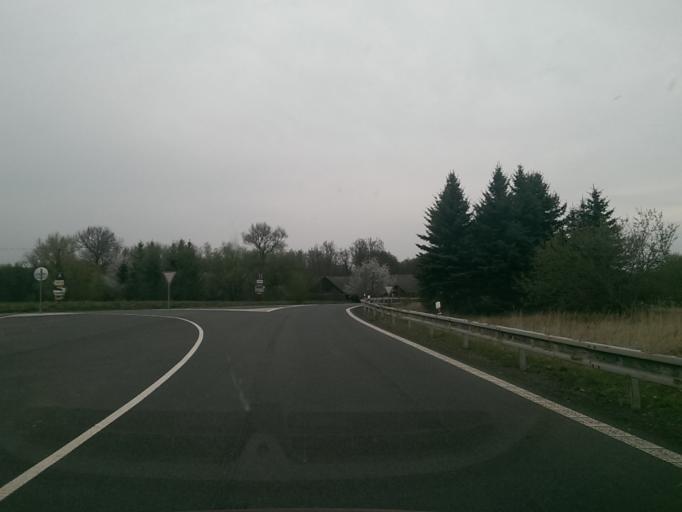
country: CZ
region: Central Bohemia
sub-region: Okres Mlada Boleslav
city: Zd'ar
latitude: 50.5461
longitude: 15.0433
